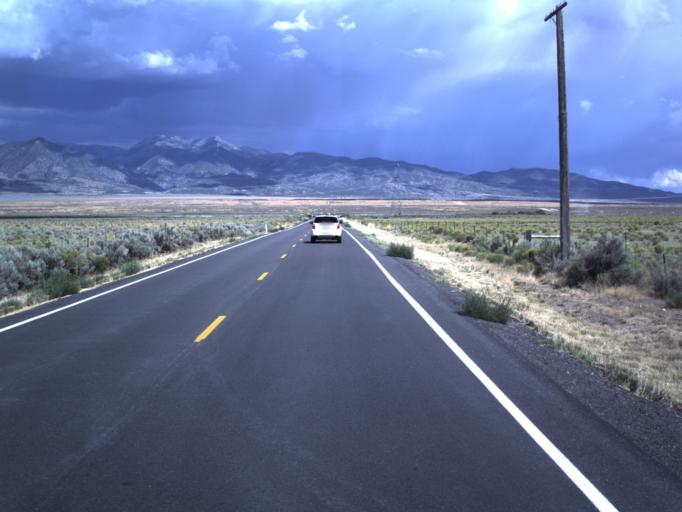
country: US
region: Utah
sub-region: Tooele County
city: Tooele
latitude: 40.3369
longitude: -112.4228
